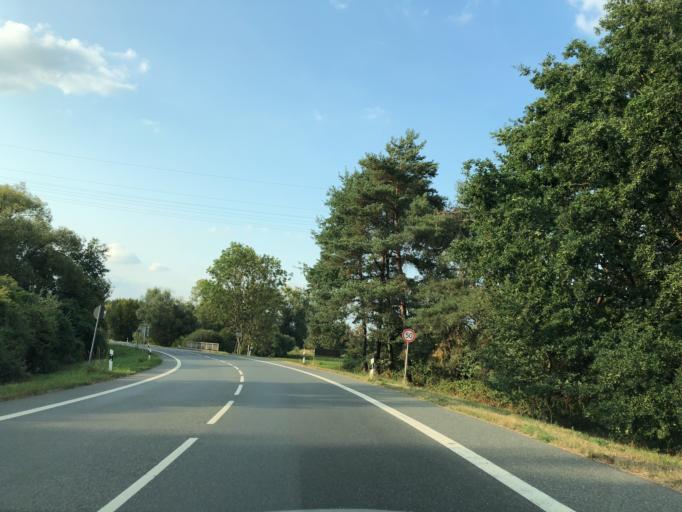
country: DE
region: Hesse
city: Obertshausen
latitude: 50.0893
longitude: 8.8629
